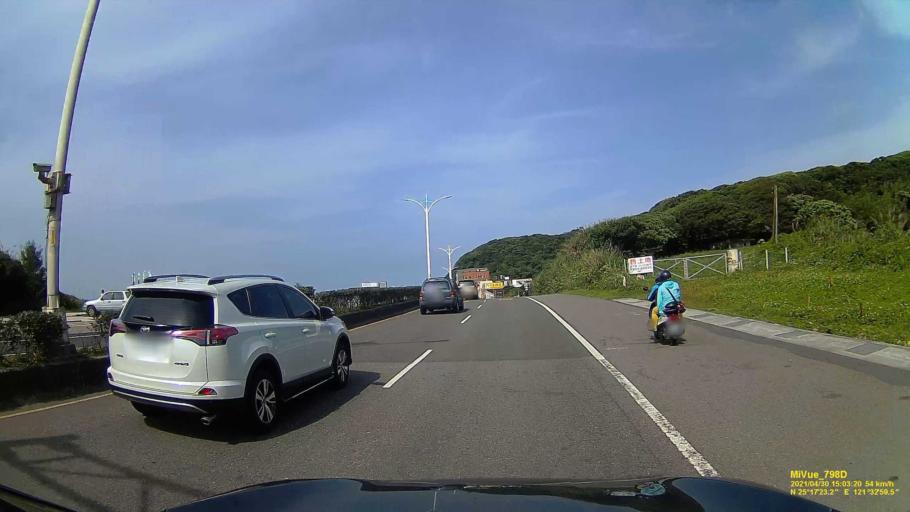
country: TW
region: Taipei
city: Taipei
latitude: 25.2899
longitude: 121.5502
